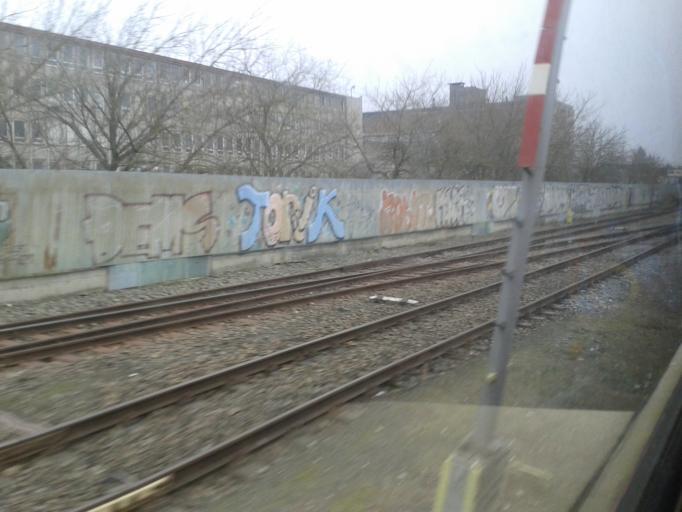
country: CZ
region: Olomoucky
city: Horka nad Moravou
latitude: 49.6152
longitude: 17.2248
